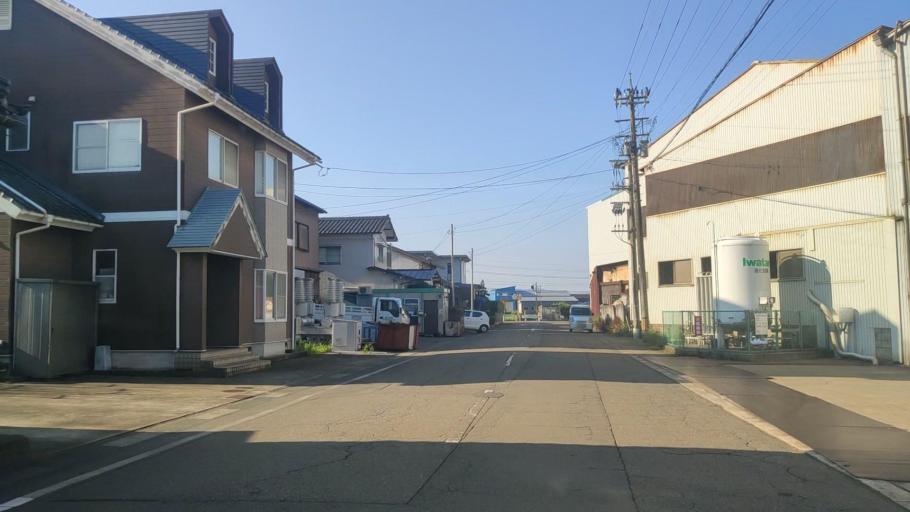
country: JP
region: Fukui
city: Fukui-shi
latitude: 36.0843
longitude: 136.2629
